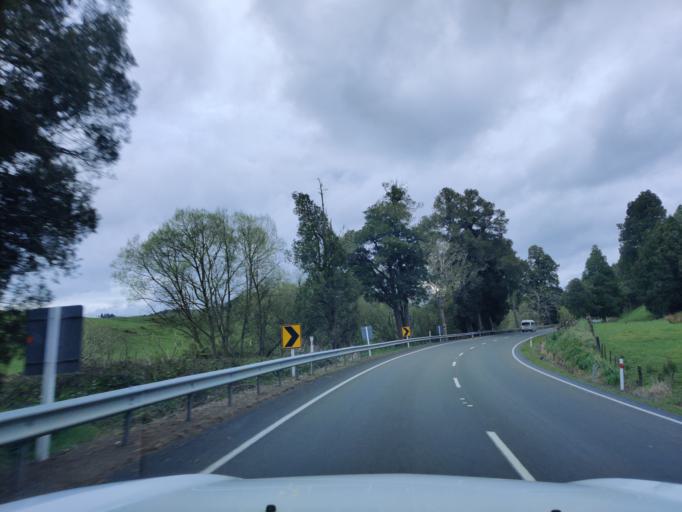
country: NZ
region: Waikato
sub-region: Otorohanga District
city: Otorohanga
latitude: -38.4833
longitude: 175.1750
